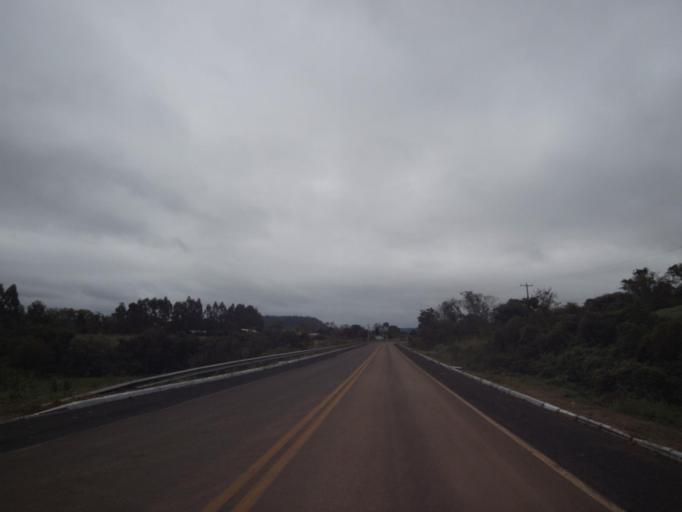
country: AR
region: Misiones
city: El Soberbio
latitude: -27.2945
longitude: -54.1901
